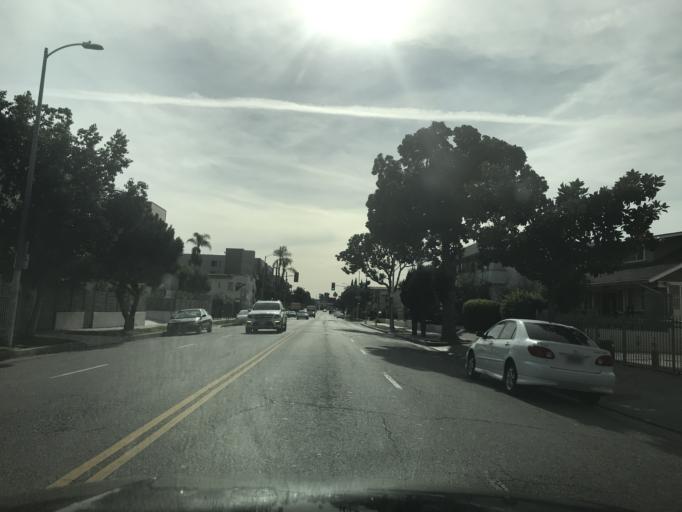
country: US
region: California
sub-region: Los Angeles County
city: Hollywood
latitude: 34.0568
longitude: -118.3143
